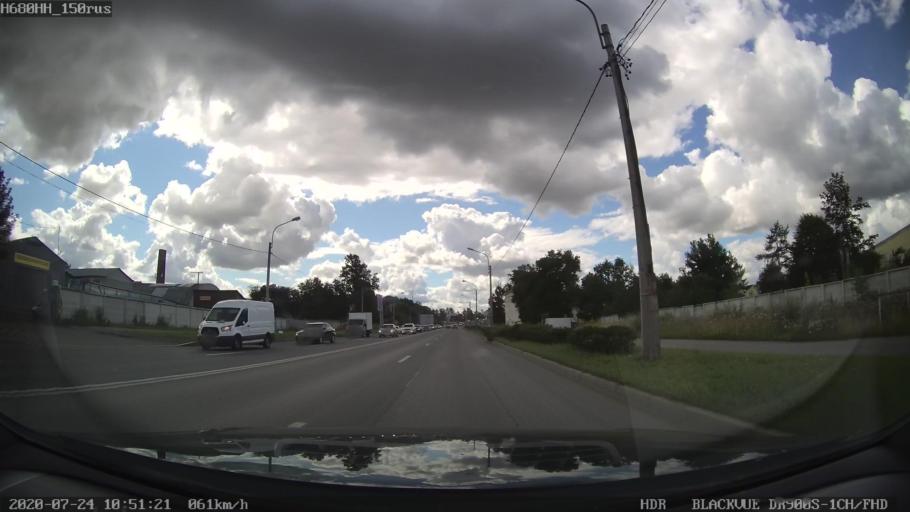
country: RU
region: St.-Petersburg
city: Admiralteisky
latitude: 59.8918
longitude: 30.3016
